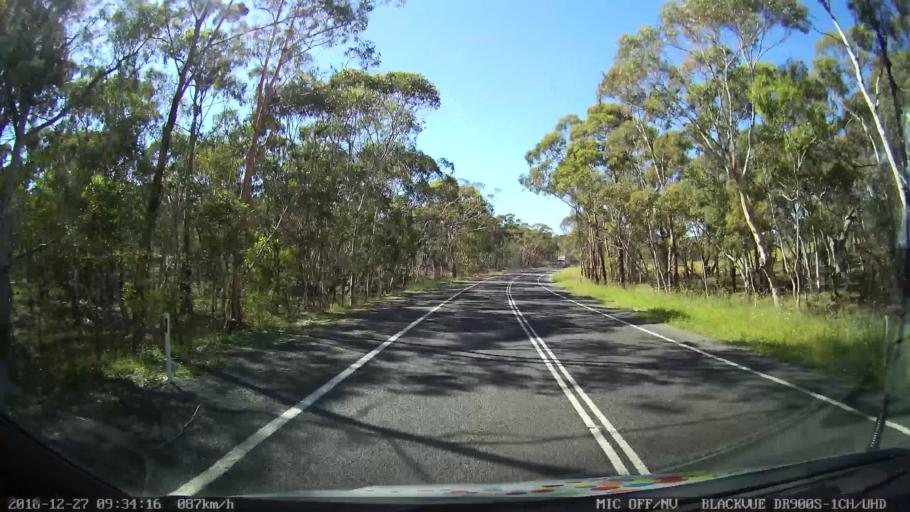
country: AU
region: New South Wales
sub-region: Lithgow
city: Portland
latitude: -33.2240
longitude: 150.0274
